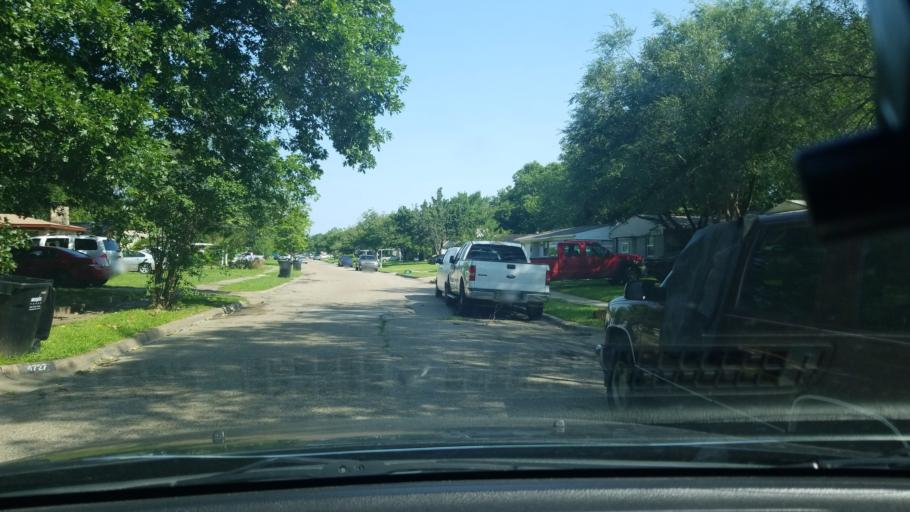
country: US
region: Texas
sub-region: Dallas County
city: Mesquite
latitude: 32.8304
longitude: -96.6402
